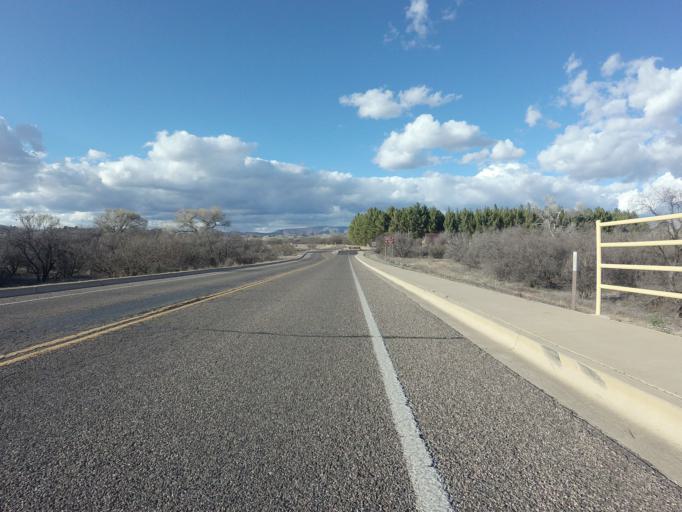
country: US
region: Arizona
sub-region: Yavapai County
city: Cottonwood
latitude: 34.7522
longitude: -112.0221
